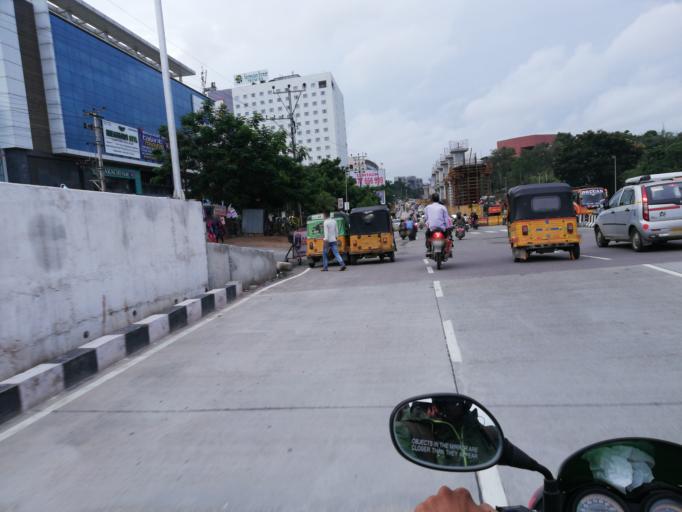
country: IN
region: Telangana
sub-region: Rangareddi
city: Kukatpalli
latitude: 17.4411
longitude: 78.3771
